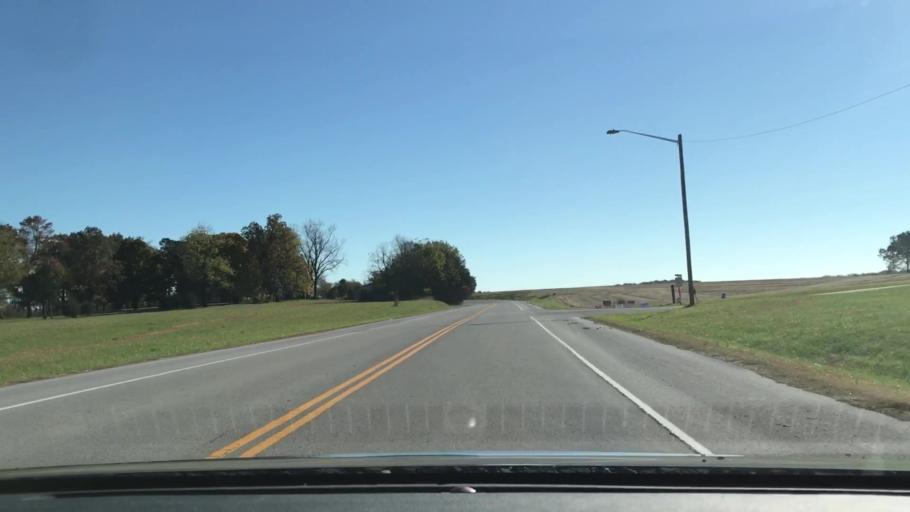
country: US
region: Kentucky
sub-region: Logan County
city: Auburn
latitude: 36.8659
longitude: -86.6985
